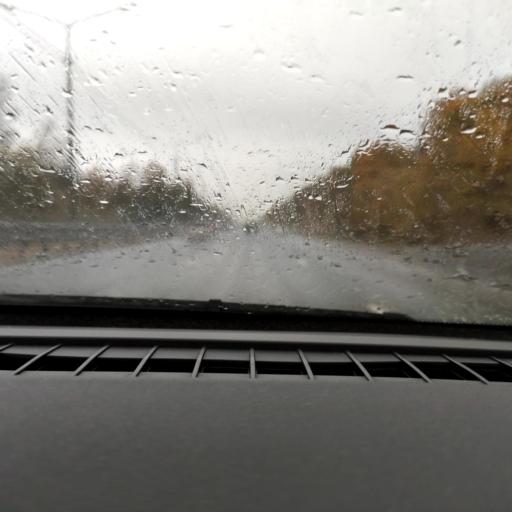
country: RU
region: Voronezj
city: Podgornoye
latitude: 51.8121
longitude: 39.2066
